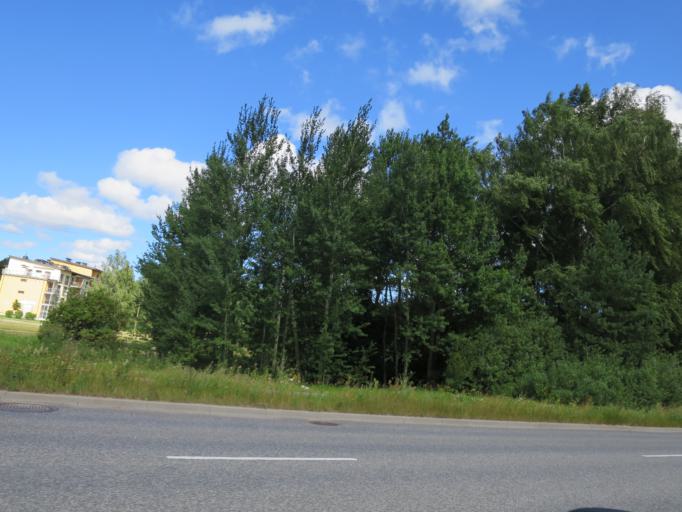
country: LV
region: Stopini
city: Ulbroka
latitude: 56.9569
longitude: 24.2457
